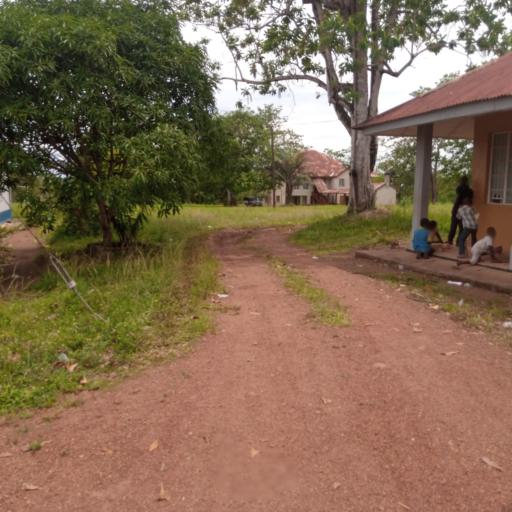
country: SL
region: Southern Province
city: Largo
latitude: 8.1097
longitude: -12.0792
